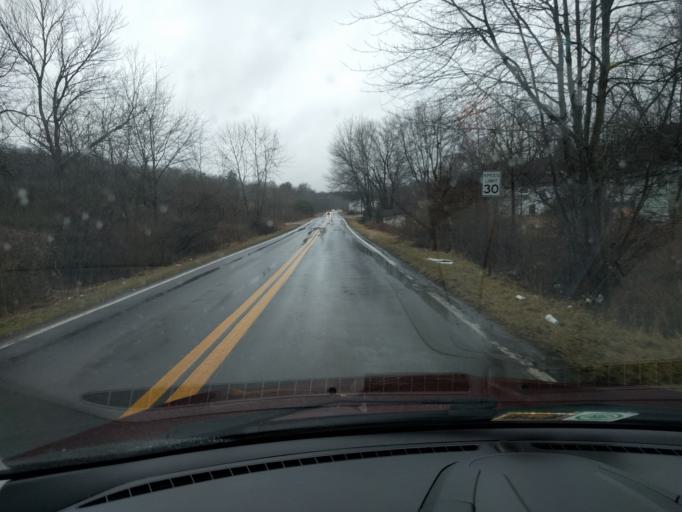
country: US
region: West Virginia
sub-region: Raleigh County
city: Beckley
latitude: 37.7905
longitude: -81.1891
